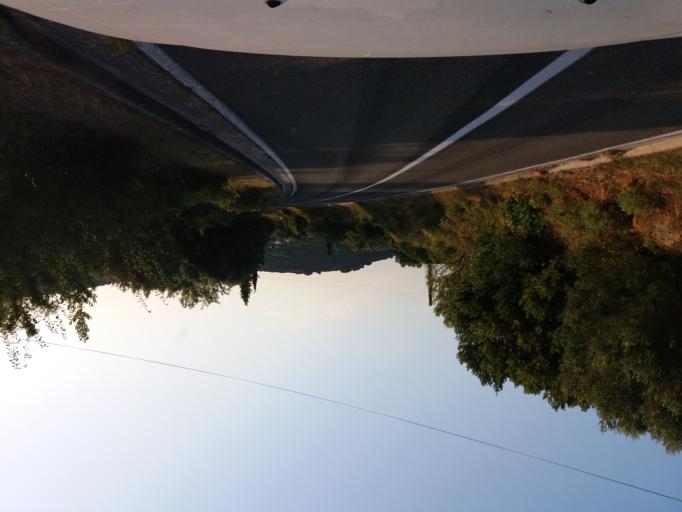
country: HR
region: Zadarska
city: Ugljan
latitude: 44.0760
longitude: 14.9965
